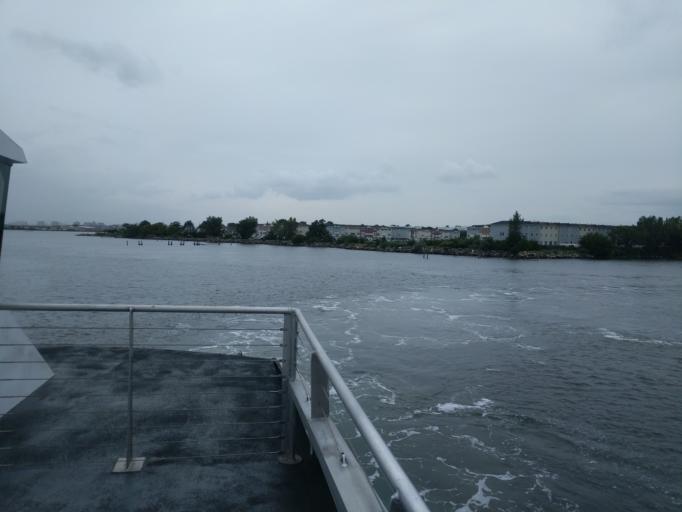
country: US
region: New York
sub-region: Bronx
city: The Bronx
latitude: 40.8032
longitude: -73.8494
